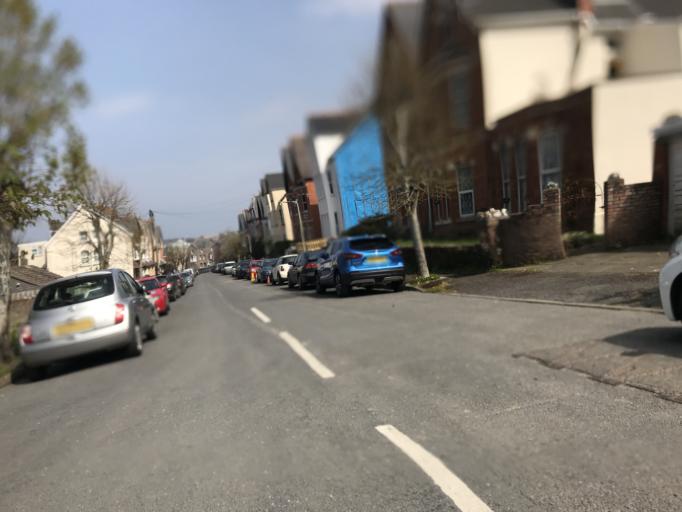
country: GB
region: England
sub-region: Devon
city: Ilfracombe
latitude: 51.2062
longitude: -4.1299
